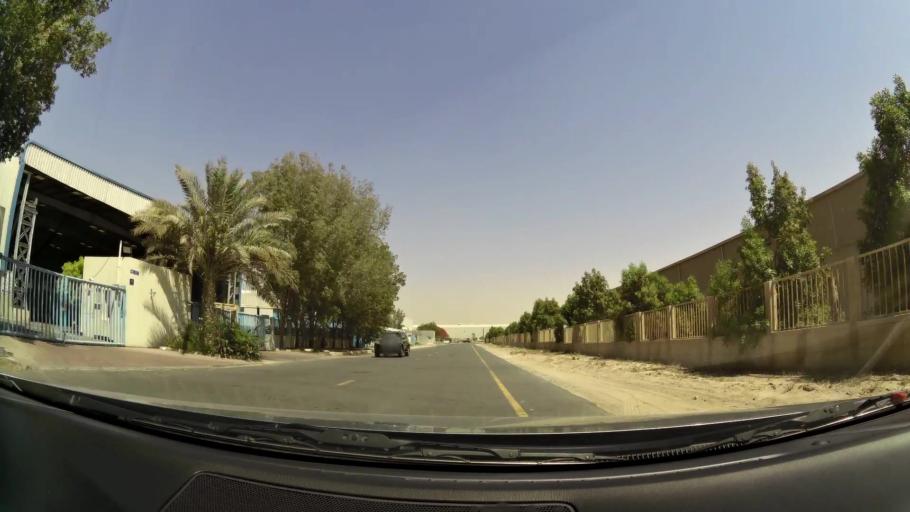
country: AE
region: Dubai
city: Dubai
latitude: 24.9882
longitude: 55.1589
